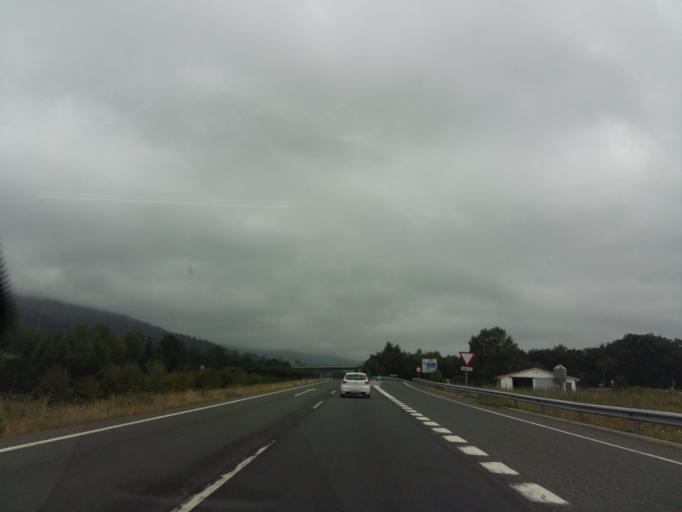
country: ES
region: Navarre
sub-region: Provincia de Navarra
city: Echarri-Aranaz
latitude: 42.8987
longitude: -2.0747
